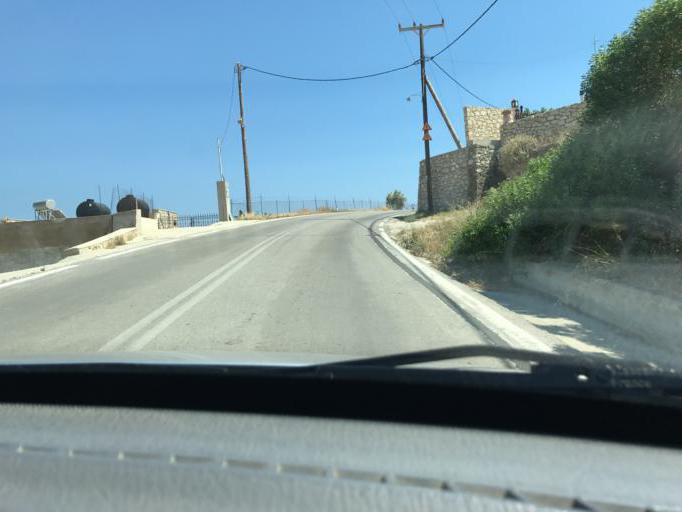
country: GR
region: South Aegean
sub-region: Nomos Dodekanisou
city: Karpathos
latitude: 35.4876
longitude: 27.1841
